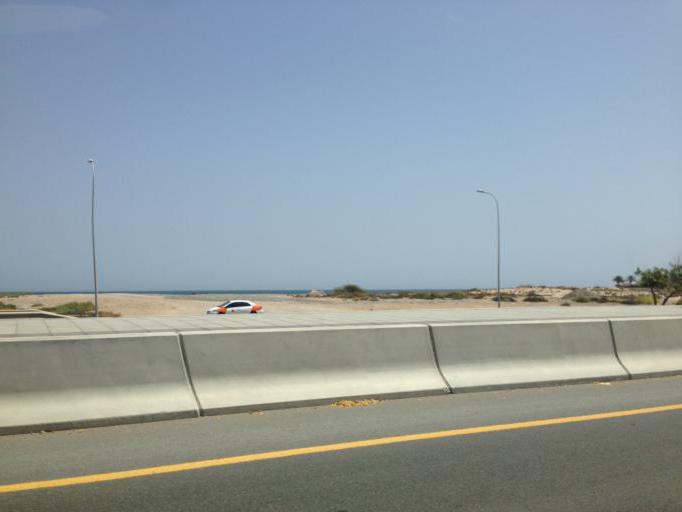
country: OM
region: Muhafazat Masqat
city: Bawshar
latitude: 23.6032
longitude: 58.3385
